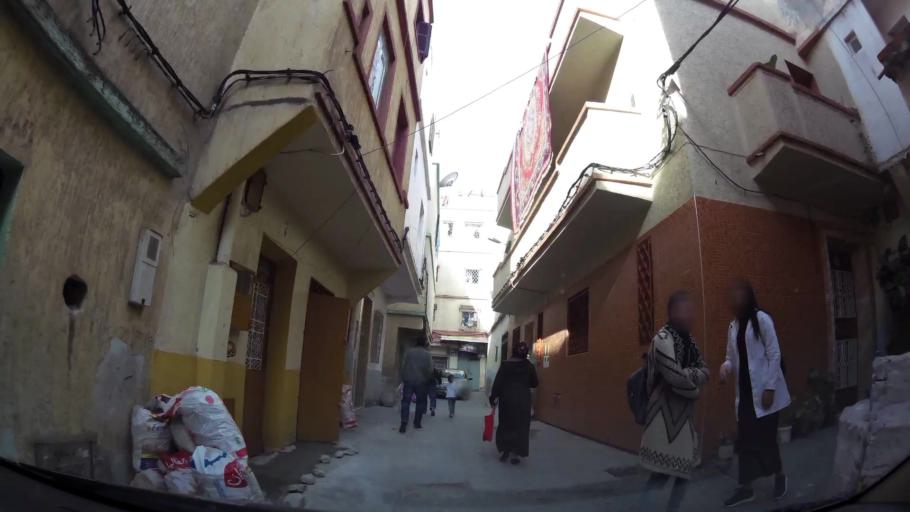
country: MA
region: Tanger-Tetouan
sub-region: Tanger-Assilah
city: Tangier
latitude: 35.7598
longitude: -5.7871
